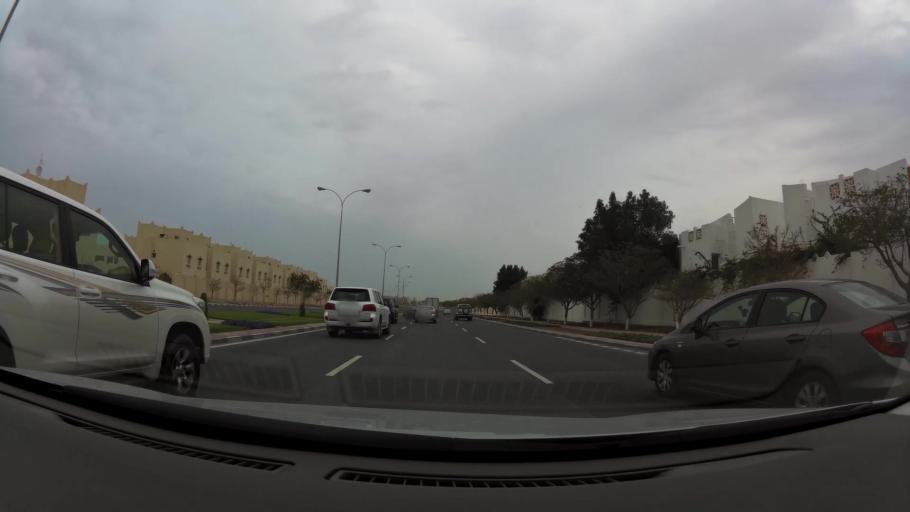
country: QA
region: Baladiyat ad Dawhah
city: Doha
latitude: 25.3298
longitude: 51.4831
